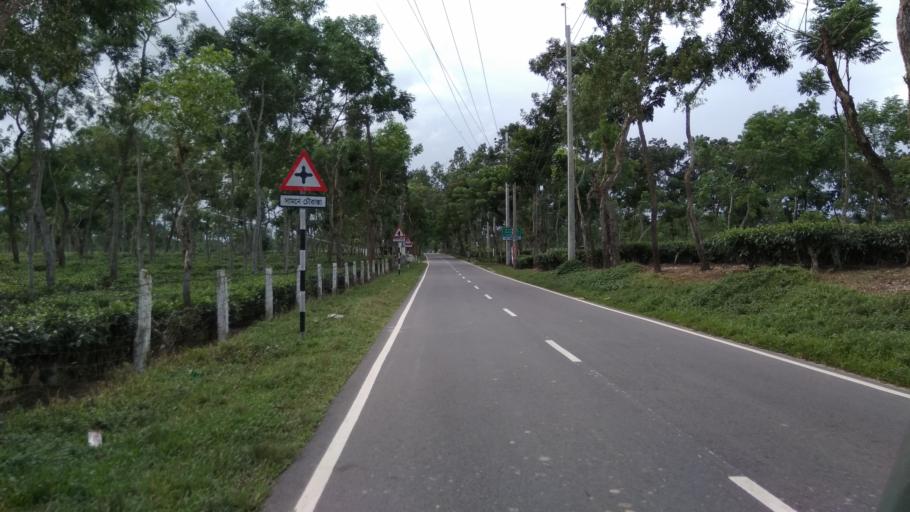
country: IN
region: Tripura
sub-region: Dhalai
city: Kamalpur
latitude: 24.3017
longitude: 91.7507
